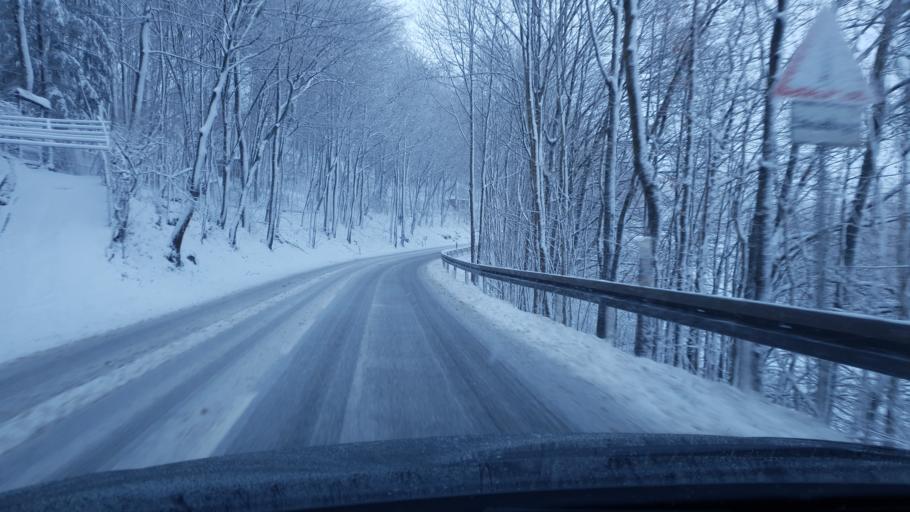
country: DE
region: Saxony
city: Wittgensdorf
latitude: 50.8986
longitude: 12.8997
